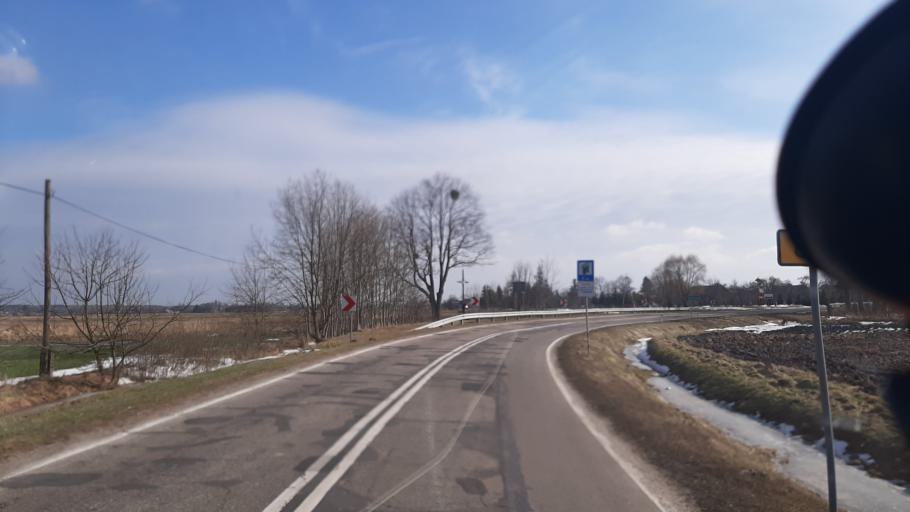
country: PL
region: Lublin Voivodeship
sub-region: Powiat wlodawski
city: Urszulin
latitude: 51.4859
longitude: 23.2841
